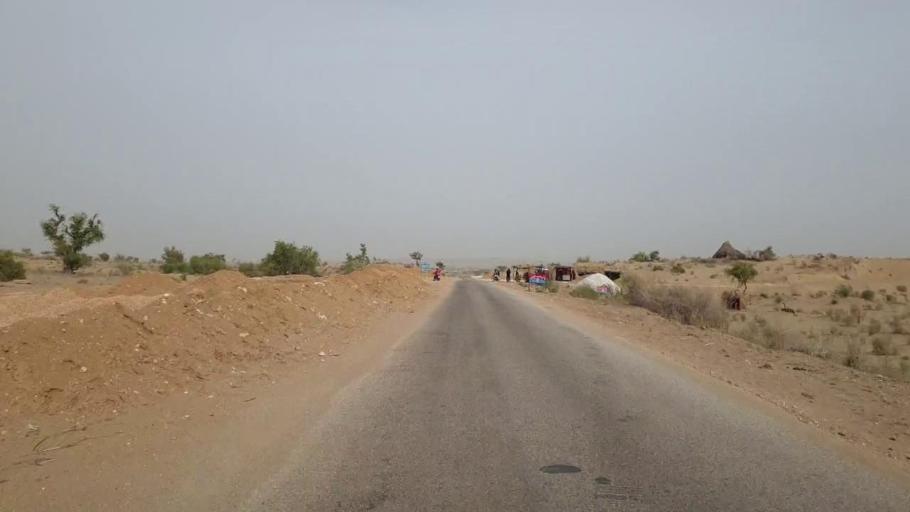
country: PK
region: Sindh
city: Islamkot
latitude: 24.5563
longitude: 70.3476
